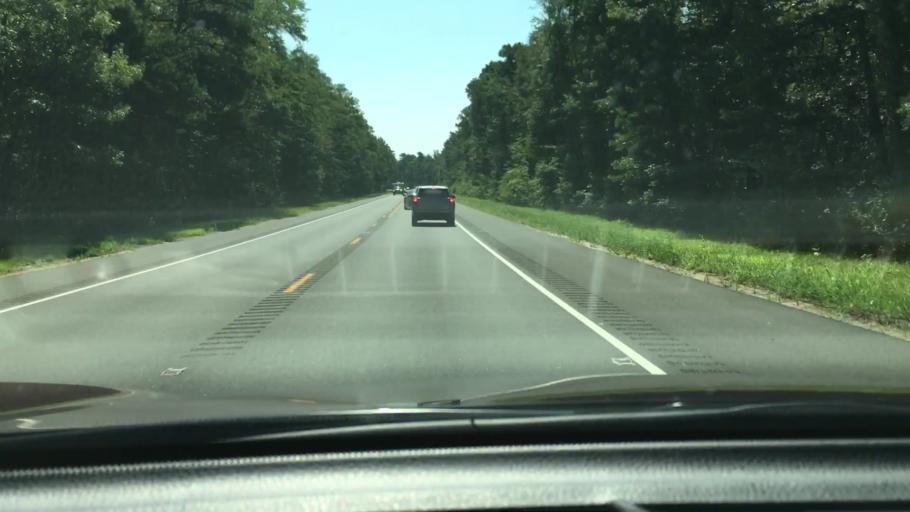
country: US
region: New Jersey
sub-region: Cape May County
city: Woodbine
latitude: 39.3273
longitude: -74.8703
